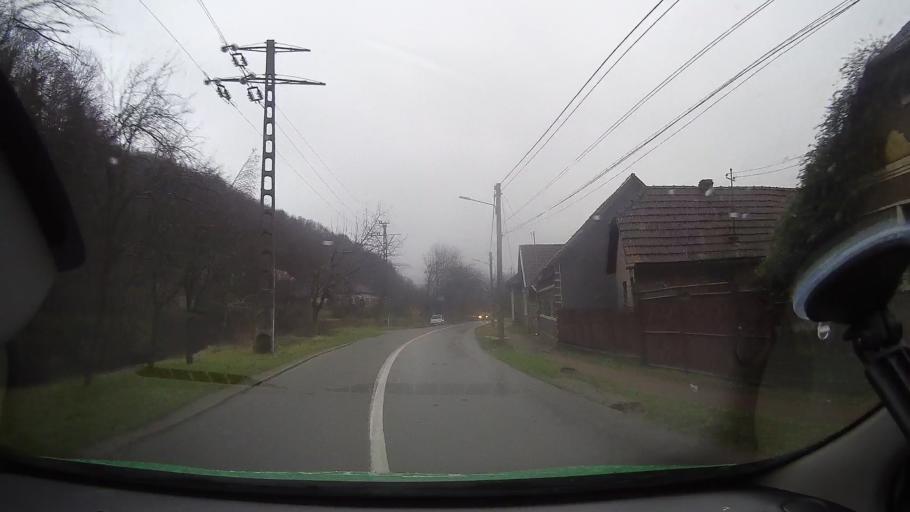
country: RO
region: Arad
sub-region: Comuna Moneasa
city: Moneasa
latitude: 46.4500
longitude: 22.2473
